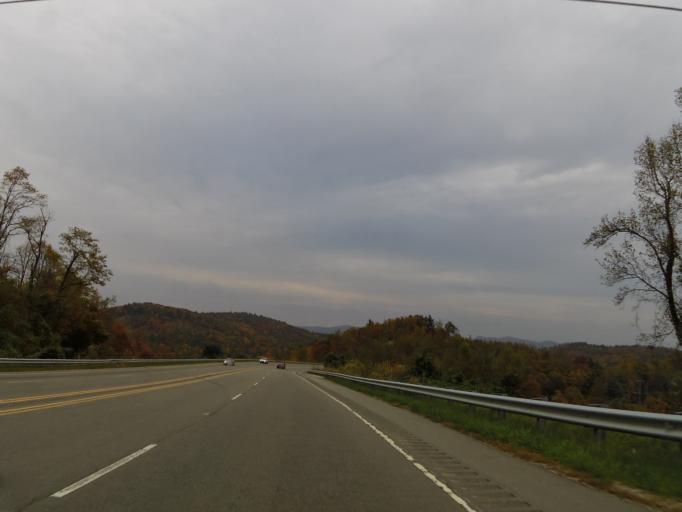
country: US
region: North Carolina
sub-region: Watauga County
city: Blowing Rock
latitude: 36.0863
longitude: -81.6323
